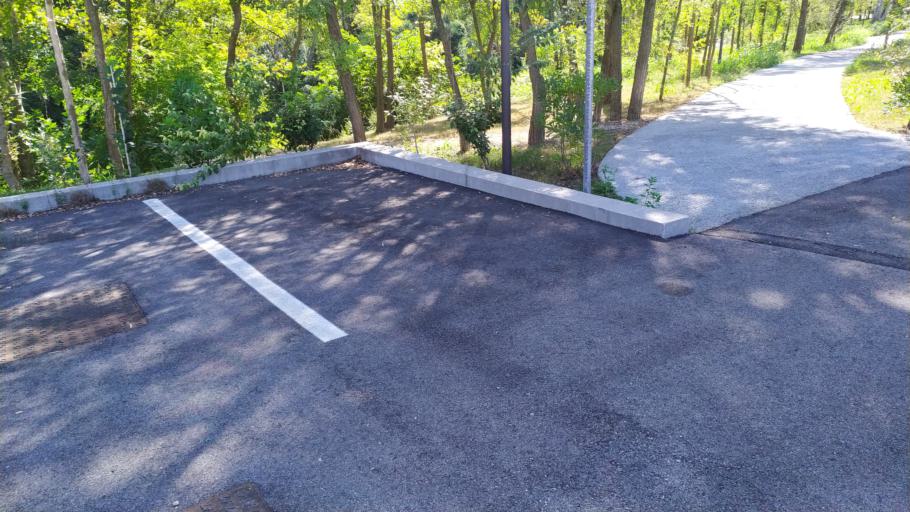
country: IT
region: Friuli Venezia Giulia
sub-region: Provincia di Pordenone
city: Sacile
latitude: 45.9462
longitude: 12.5005
